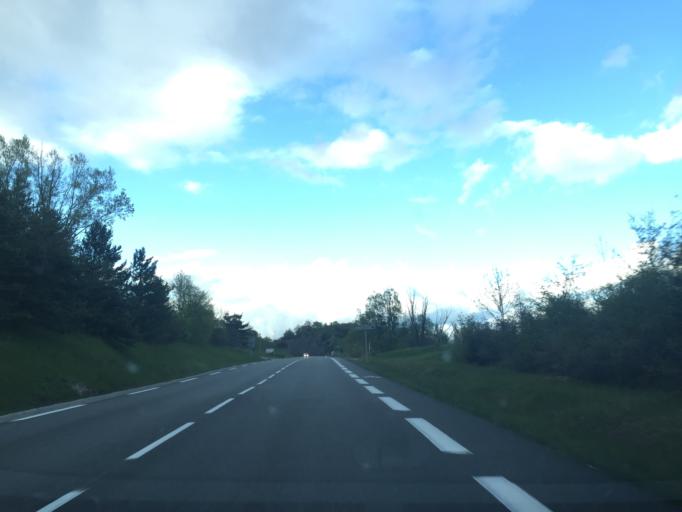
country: FR
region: Rhone-Alpes
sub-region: Departement de l'Isere
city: Mens
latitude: 44.7927
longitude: 5.6342
